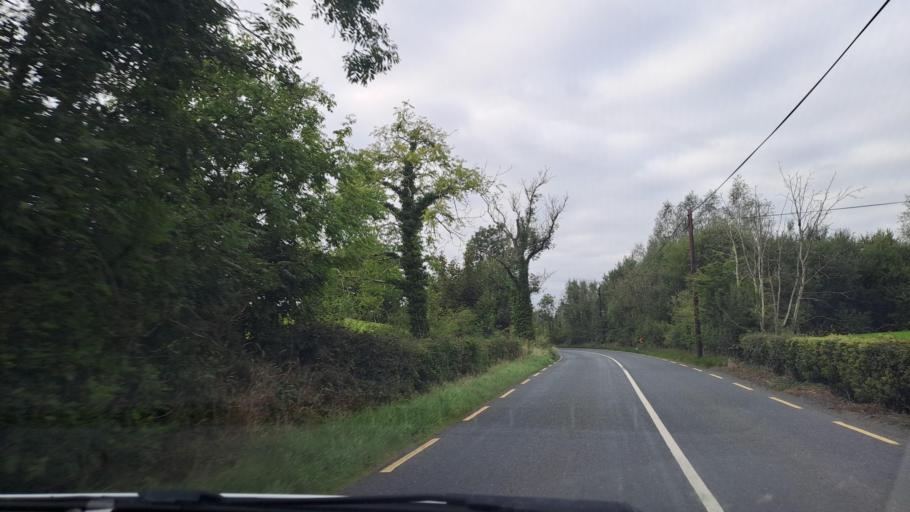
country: IE
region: Ulster
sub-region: County Monaghan
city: Carrickmacross
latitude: 54.0146
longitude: -6.7589
